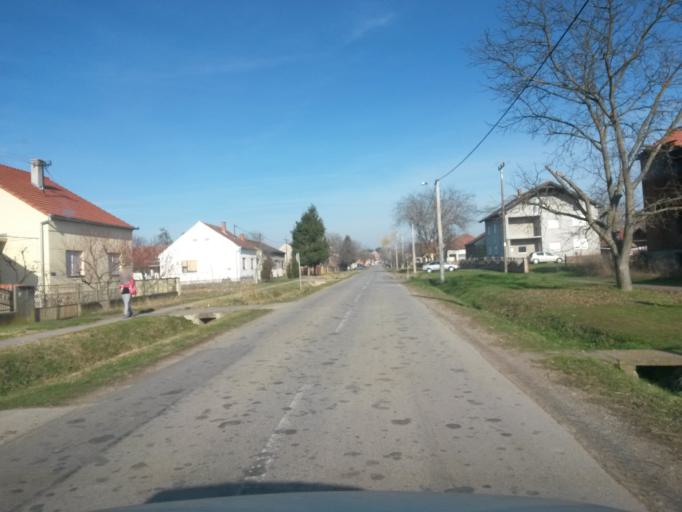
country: HR
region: Vukovarsko-Srijemska
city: Slakovci
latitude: 45.2482
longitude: 18.9033
